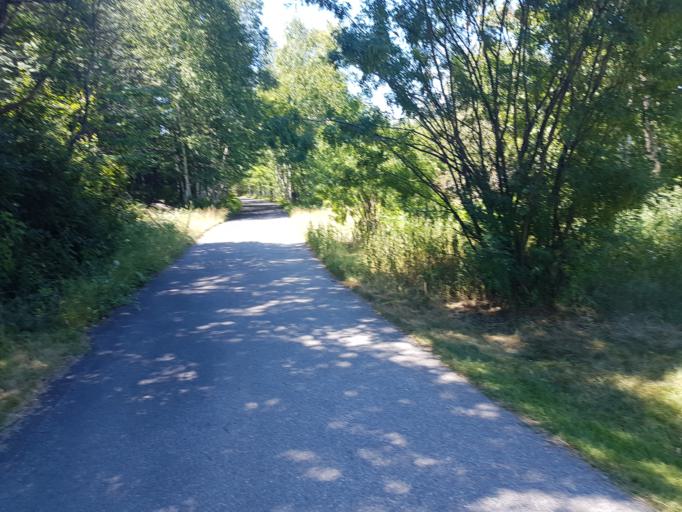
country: CA
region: Quebec
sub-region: Abitibi-Temiscamingue
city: Temiscaming
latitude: 46.7208
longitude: -79.0938
